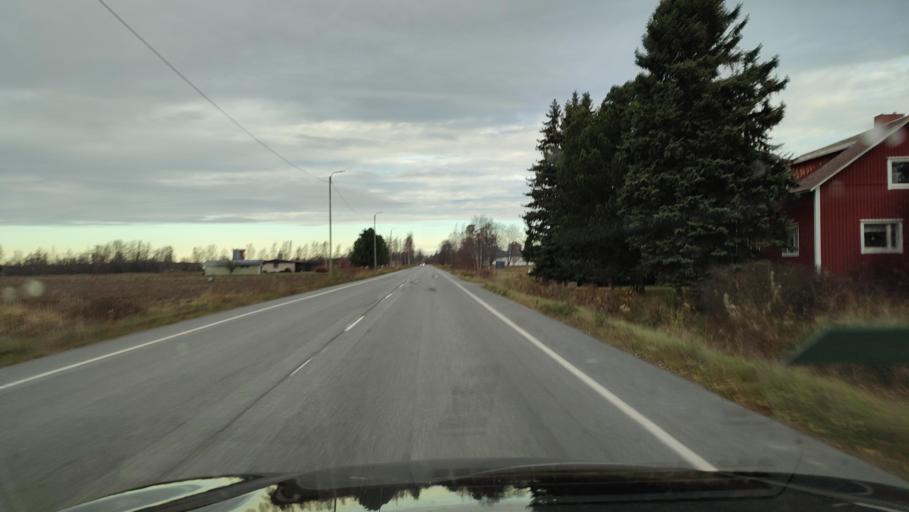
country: FI
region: Ostrobothnia
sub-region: Sydosterbotten
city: Naerpes
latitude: 62.4544
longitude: 21.3535
